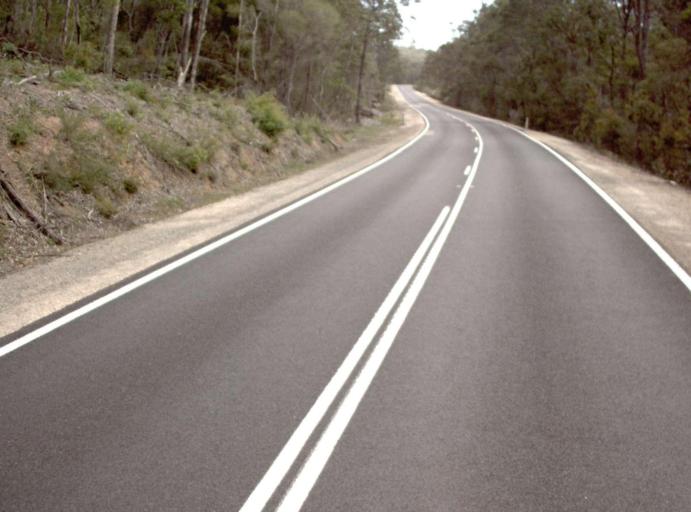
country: AU
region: New South Wales
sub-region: Bega Valley
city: Eden
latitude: -37.4505
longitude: 149.6205
